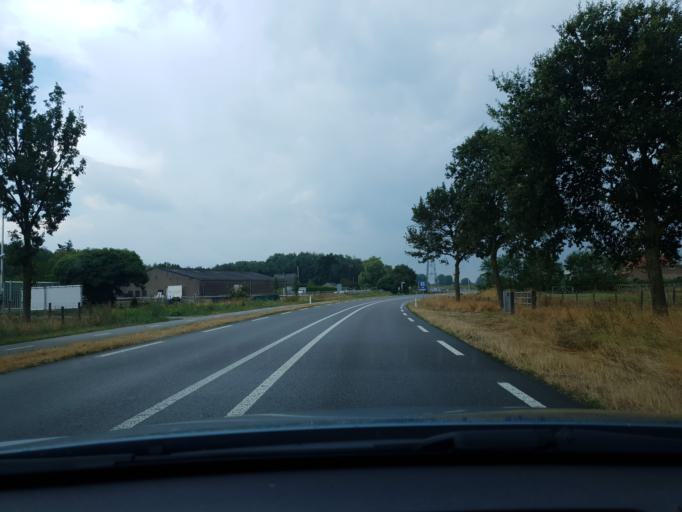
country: NL
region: North Brabant
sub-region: Gemeente Cuijk
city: Cuijk
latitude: 51.7671
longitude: 5.8351
